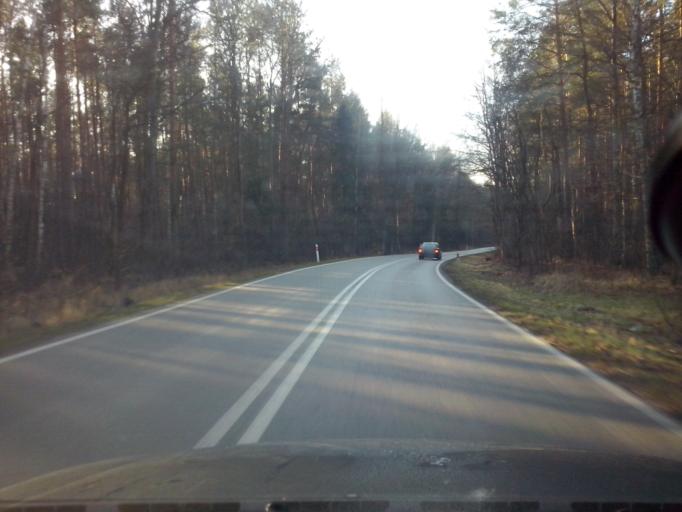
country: PL
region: Subcarpathian Voivodeship
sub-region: Powiat nizanski
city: Bieliny
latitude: 50.3939
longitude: 22.2804
